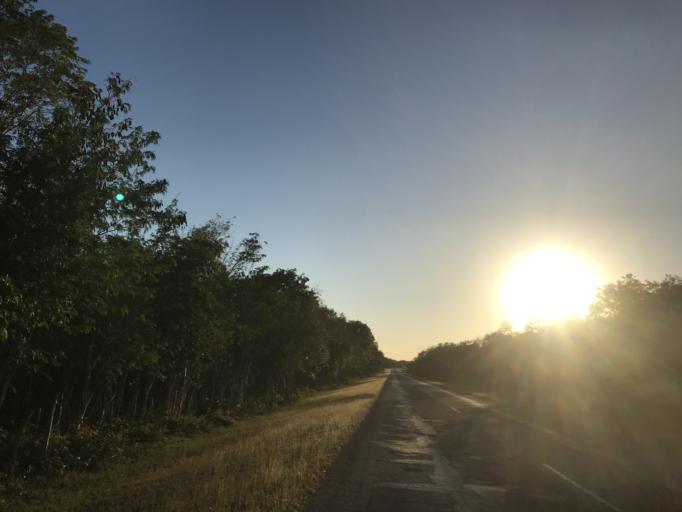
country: CU
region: Cienfuegos
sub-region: Municipio de Aguada de Pasajeros
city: Aguada de Pasajeros
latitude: 22.0705
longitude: -81.0374
